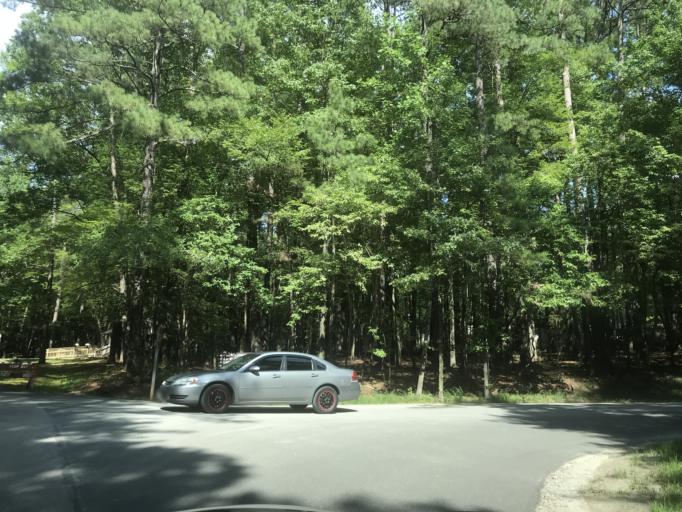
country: US
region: North Carolina
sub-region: Wake County
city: Morrisville
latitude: 35.8782
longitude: -78.7577
